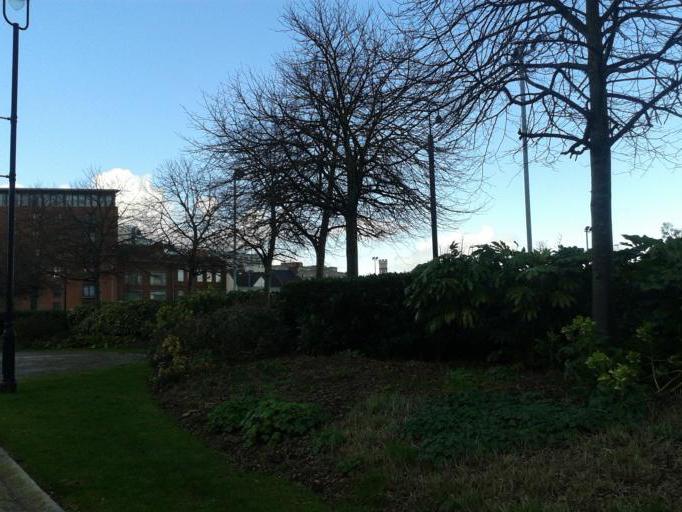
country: GB
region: Northern Ireland
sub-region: City of Belfast
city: Belfast
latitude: 54.5918
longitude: -5.9245
